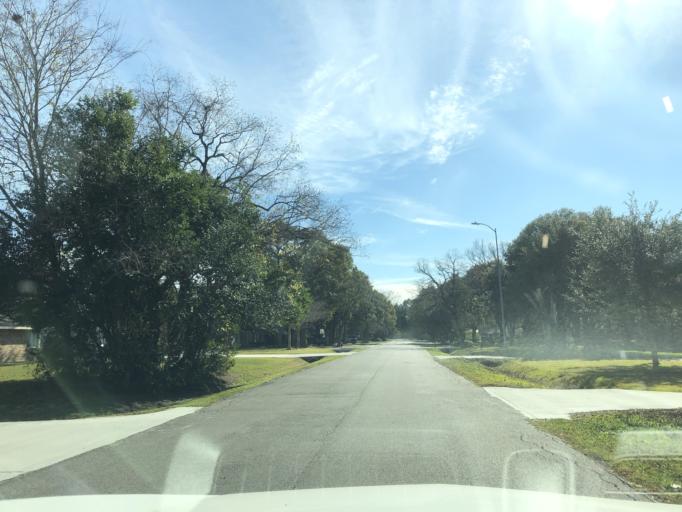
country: US
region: Texas
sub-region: Harris County
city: Bellaire
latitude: 29.6818
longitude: -95.5130
